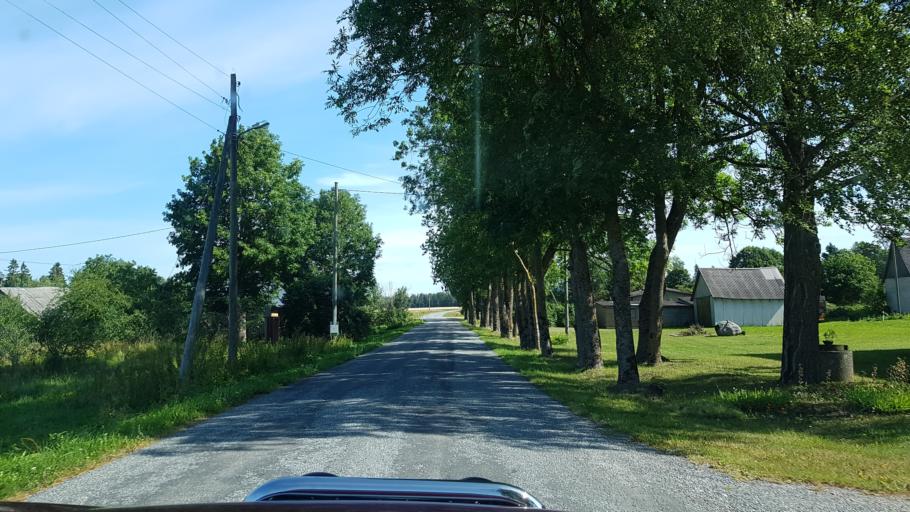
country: EE
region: Jaervamaa
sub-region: Jaerva-Jaani vald
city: Jarva-Jaani
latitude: 59.1146
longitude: 25.7883
